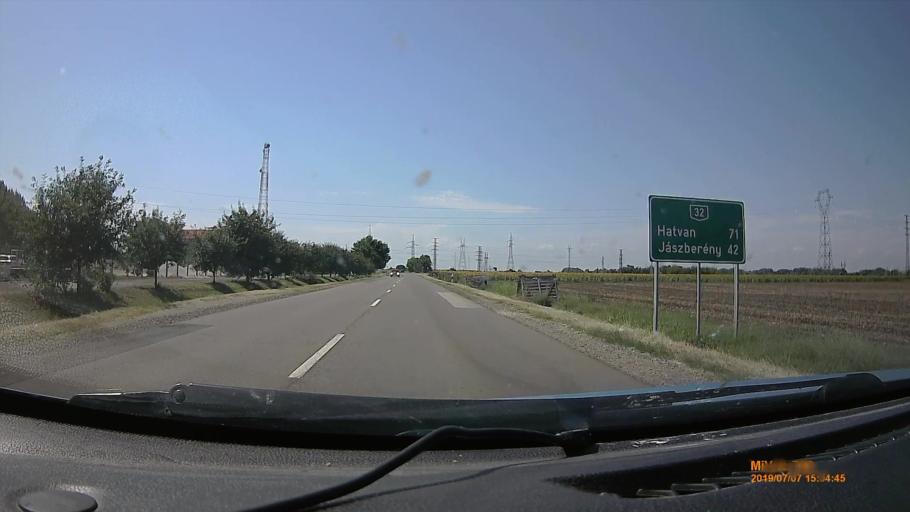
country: HU
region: Jasz-Nagykun-Szolnok
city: Szolnok
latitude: 47.2035
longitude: 20.1552
